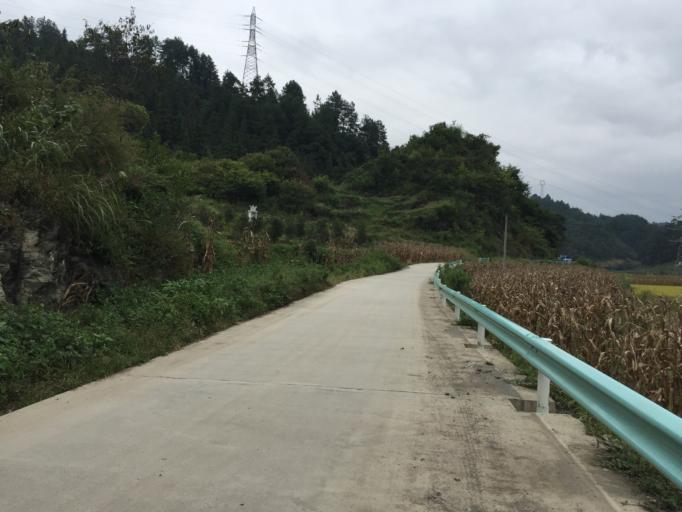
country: CN
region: Guizhou Sheng
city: Duyun
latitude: 26.3413
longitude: 107.5360
